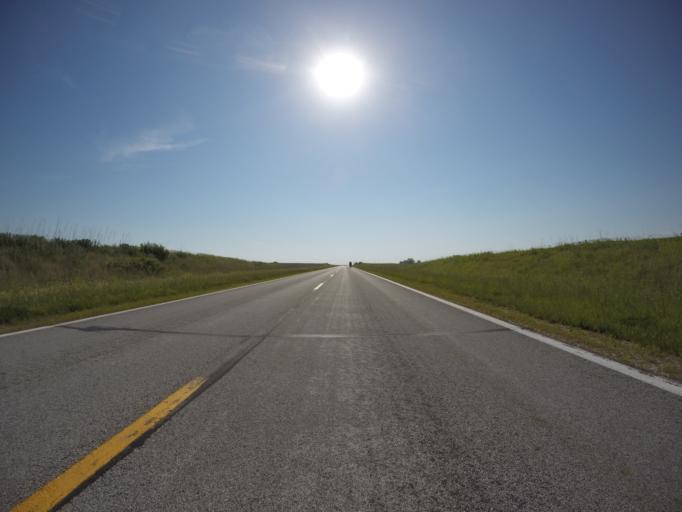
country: US
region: Nebraska
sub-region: Pawnee County
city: Pawnee City
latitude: 40.0447
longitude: -96.3754
